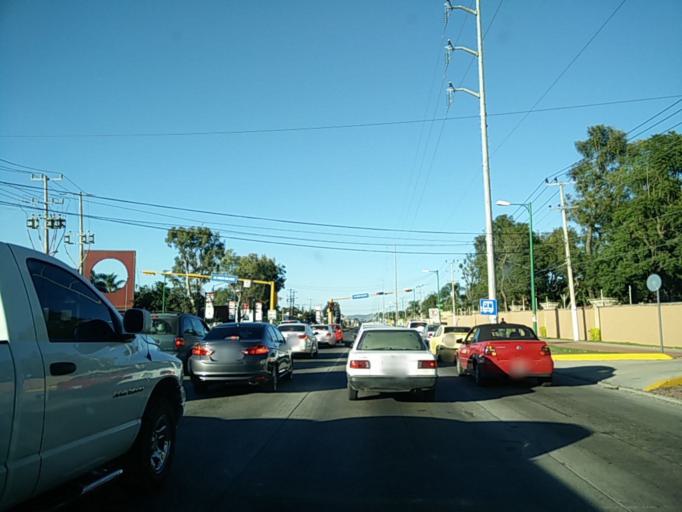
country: MX
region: Jalisco
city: Nuevo Mexico
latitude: 20.7249
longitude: -103.4533
